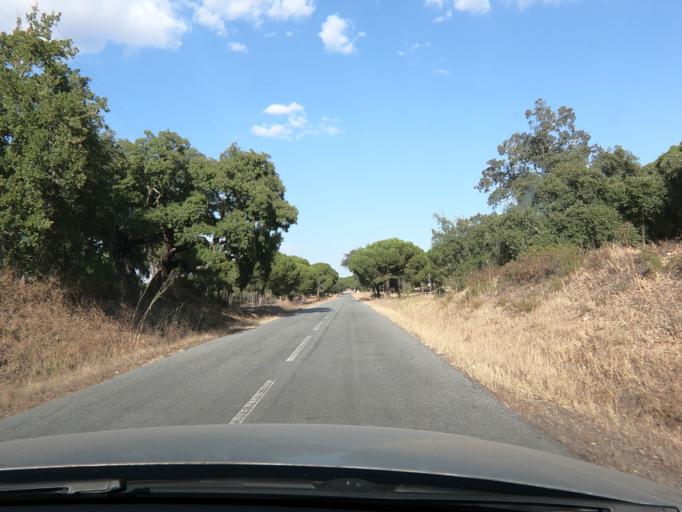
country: PT
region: Setubal
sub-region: Alcacer do Sal
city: Alcacer do Sal
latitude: 38.2629
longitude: -8.3512
